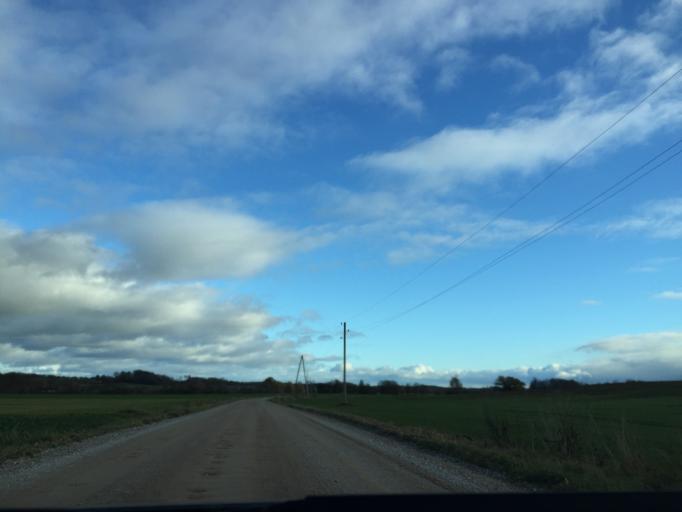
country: LV
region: Jaunpils
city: Jaunpils
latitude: 56.9203
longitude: 22.9545
